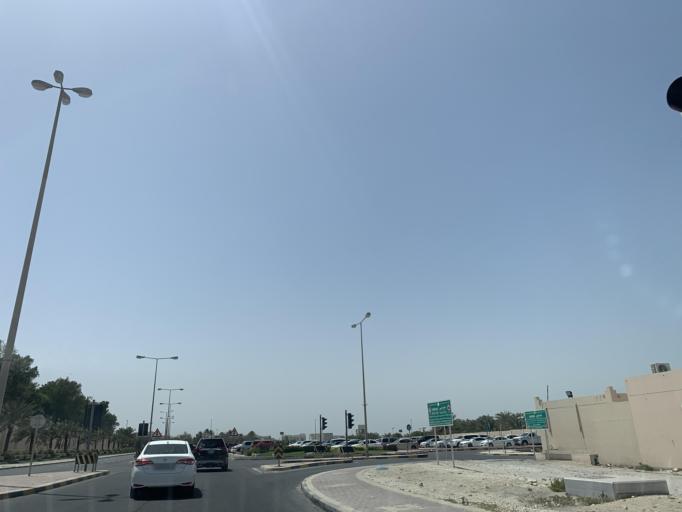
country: BH
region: Northern
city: Ar Rifa'
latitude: 26.1414
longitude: 50.5460
